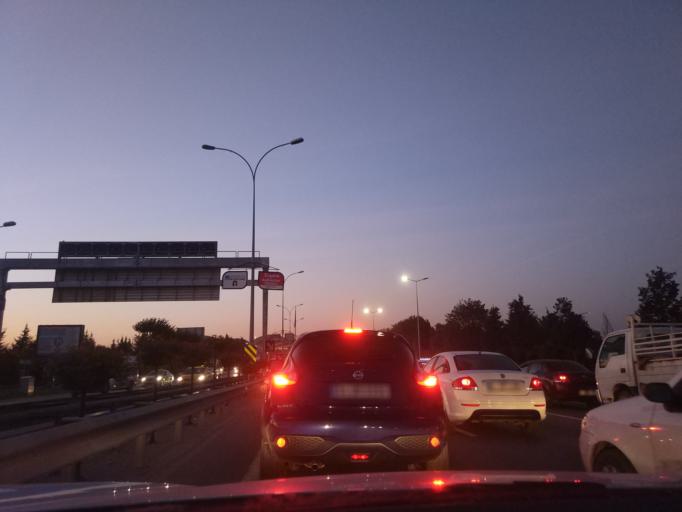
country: TR
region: Istanbul
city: Pendik
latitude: 40.9137
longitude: 29.3128
